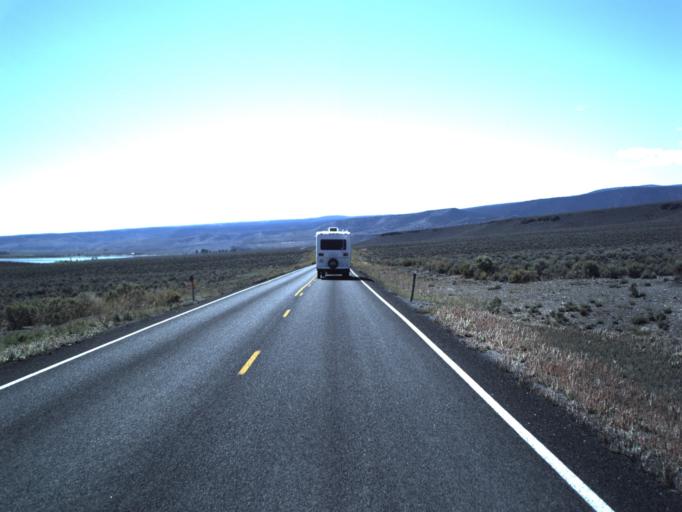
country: US
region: Utah
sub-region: Piute County
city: Junction
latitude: 38.2007
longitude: -112.0081
